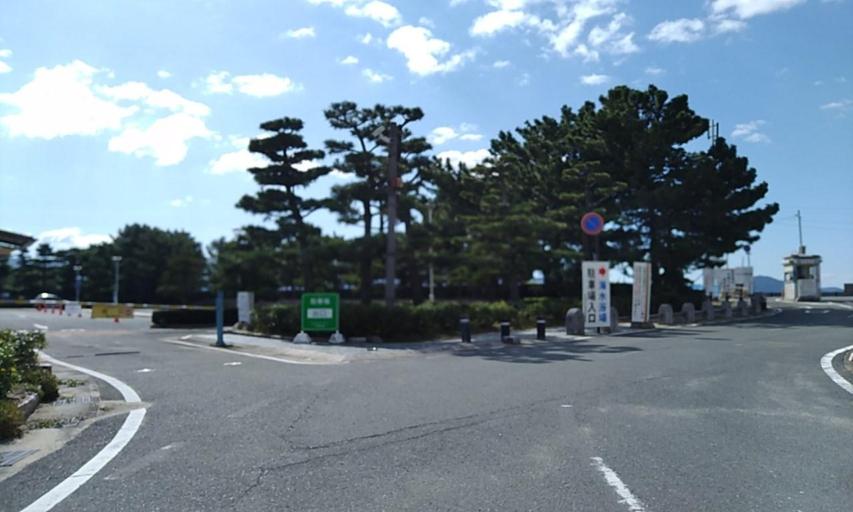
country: JP
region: Wakayama
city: Minato
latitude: 34.1832
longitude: 135.1719
